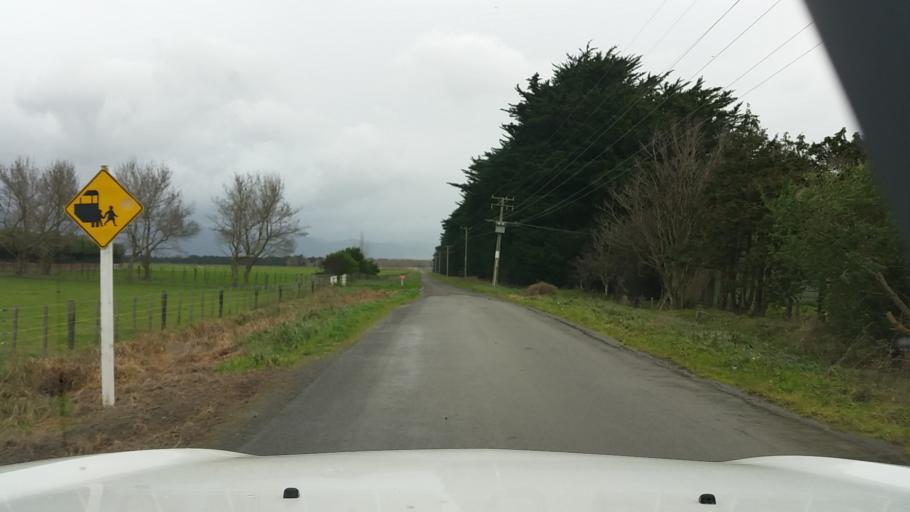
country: NZ
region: Wellington
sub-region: Upper Hutt City
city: Upper Hutt
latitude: -41.3281
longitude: 175.2124
